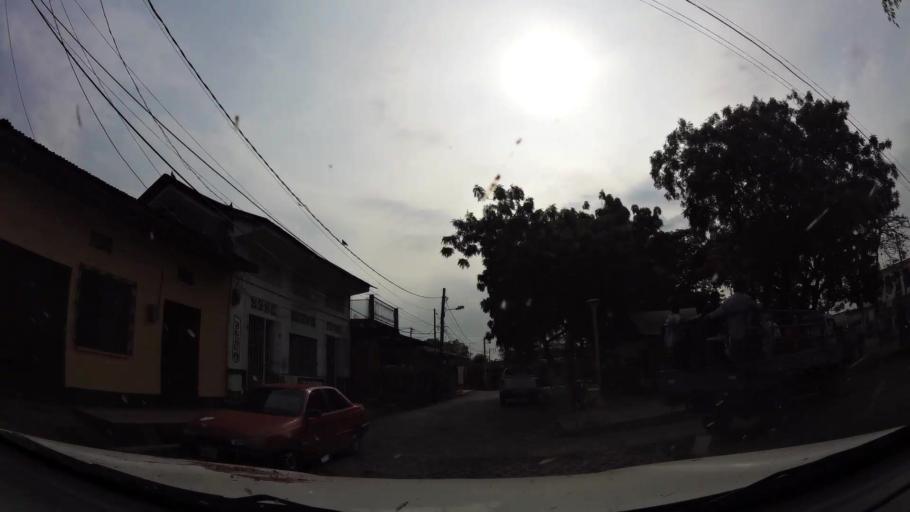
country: NI
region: Masaya
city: Masaya
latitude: 11.9732
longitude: -86.0915
